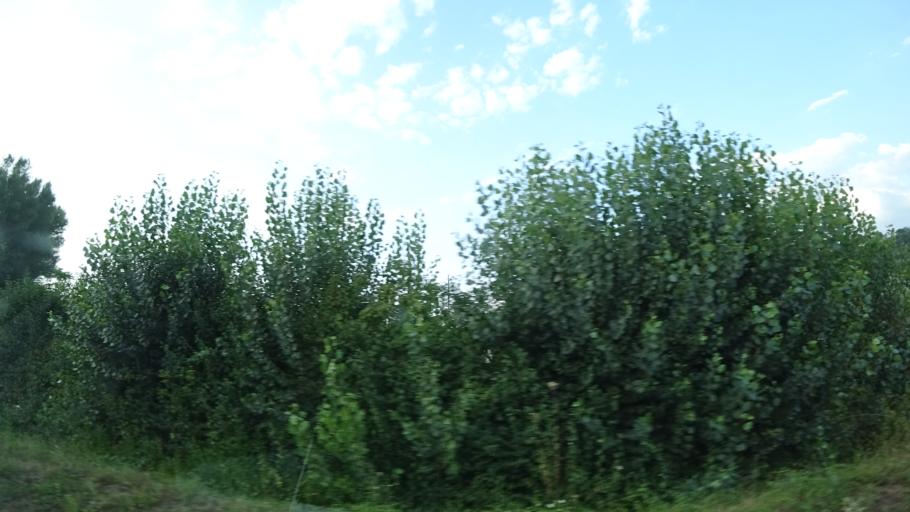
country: FR
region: Midi-Pyrenees
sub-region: Departement de l'Aveyron
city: Livinhac-le-Haut
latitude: 44.6029
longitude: 2.2408
